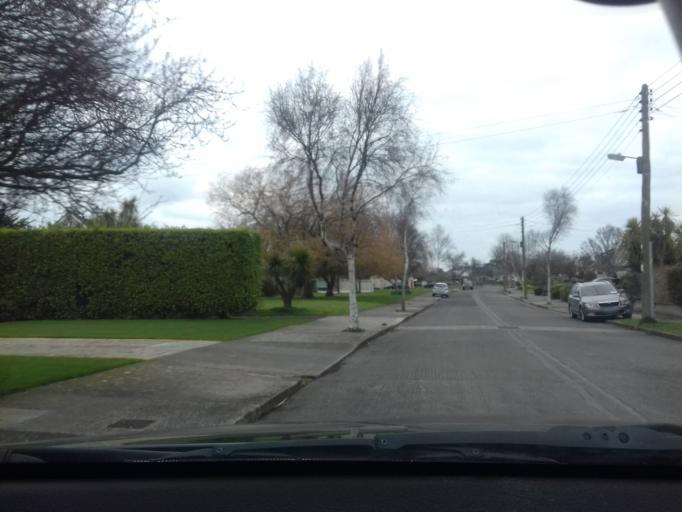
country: IE
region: Leinster
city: Sutton
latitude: 53.3862
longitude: -6.0946
